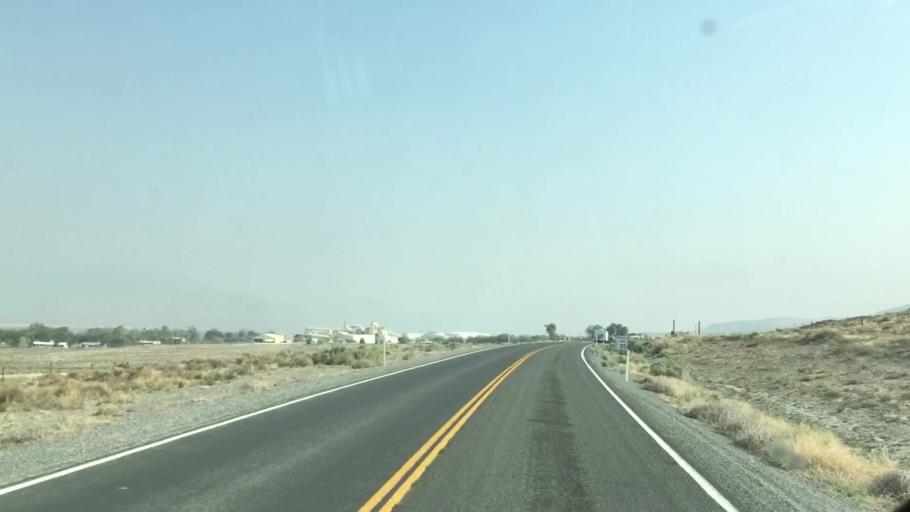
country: US
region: Nevada
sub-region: Pershing County
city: Lovelock
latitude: 40.5687
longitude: -119.3385
